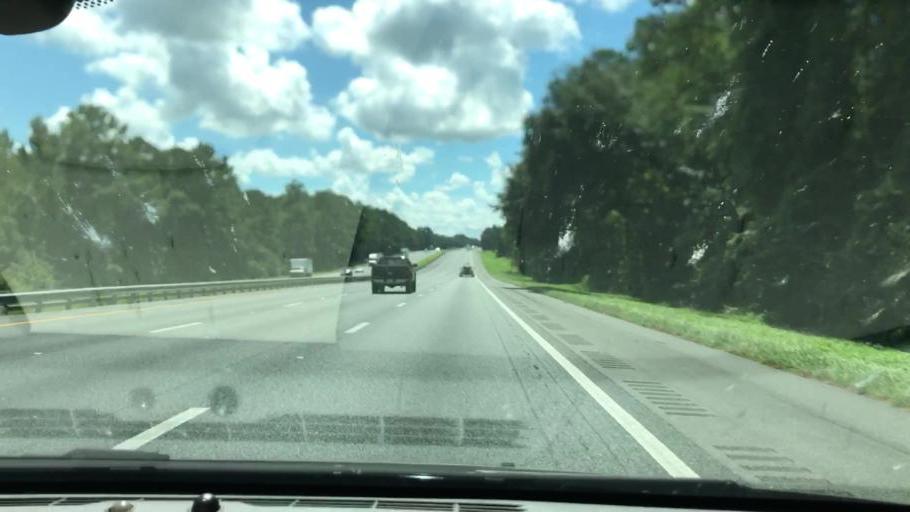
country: US
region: Florida
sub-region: Alachua County
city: High Springs
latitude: 29.9709
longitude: -82.5758
